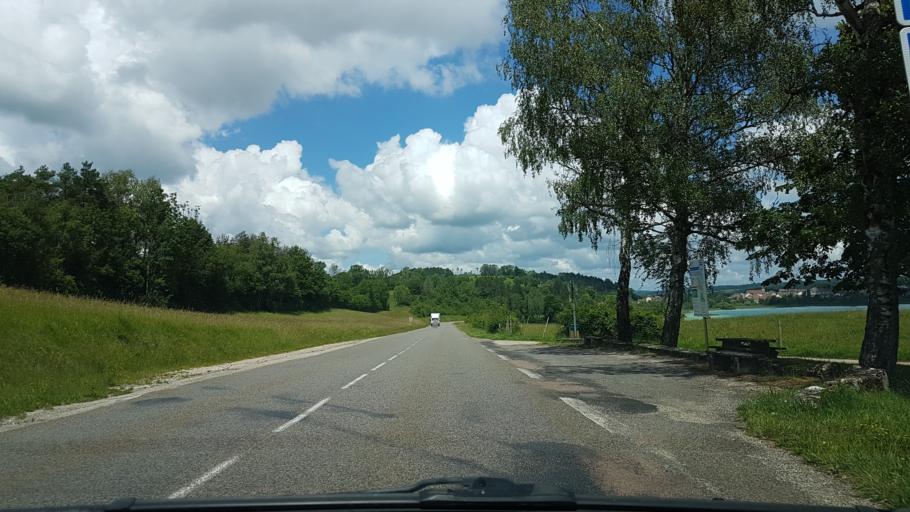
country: FR
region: Franche-Comte
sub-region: Departement du Jura
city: Clairvaux-les-Lacs
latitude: 46.5598
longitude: 5.7447
